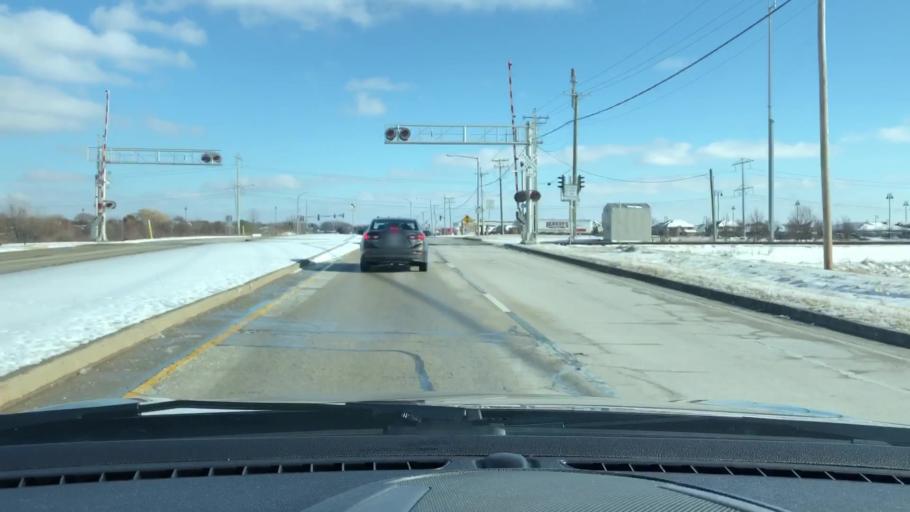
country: US
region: Illinois
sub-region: Will County
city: New Lenox
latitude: 41.4831
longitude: -87.9605
